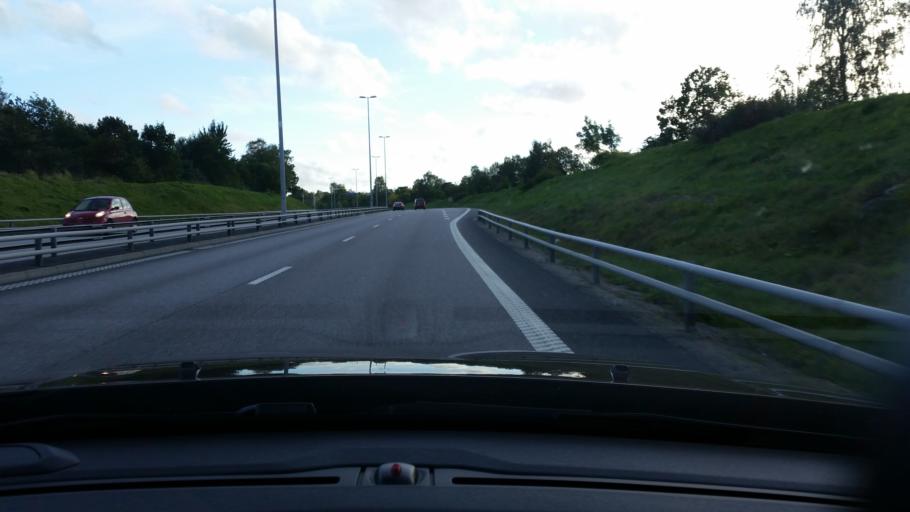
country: SE
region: Vaestra Goetaland
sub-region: Trollhattan
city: Trollhattan
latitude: 58.2604
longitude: 12.2868
